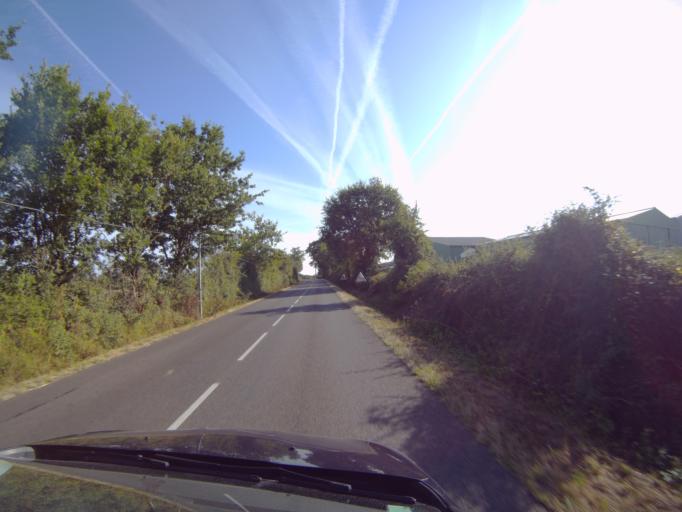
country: FR
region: Pays de la Loire
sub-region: Departement de la Vendee
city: Nieul-le-Dolent
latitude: 46.5545
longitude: -1.5231
